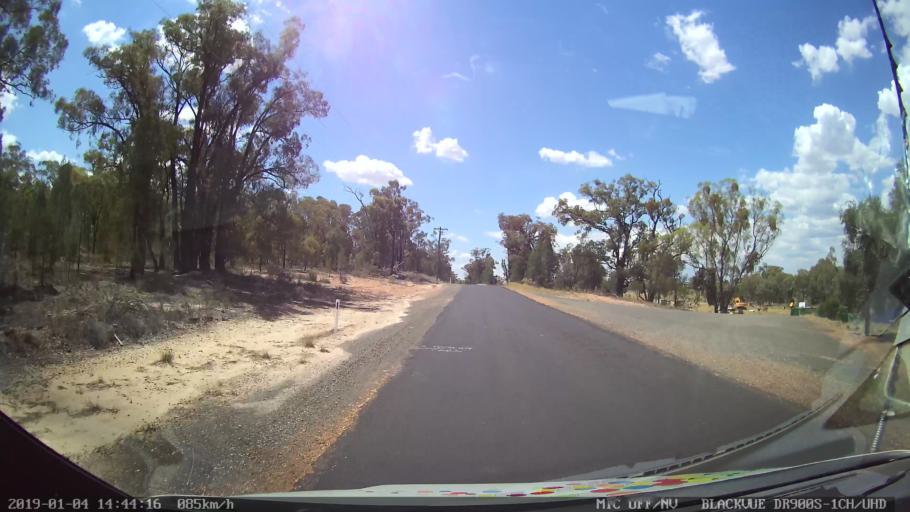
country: AU
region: New South Wales
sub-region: Dubbo Municipality
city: Dubbo
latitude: -32.1084
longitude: 148.6553
